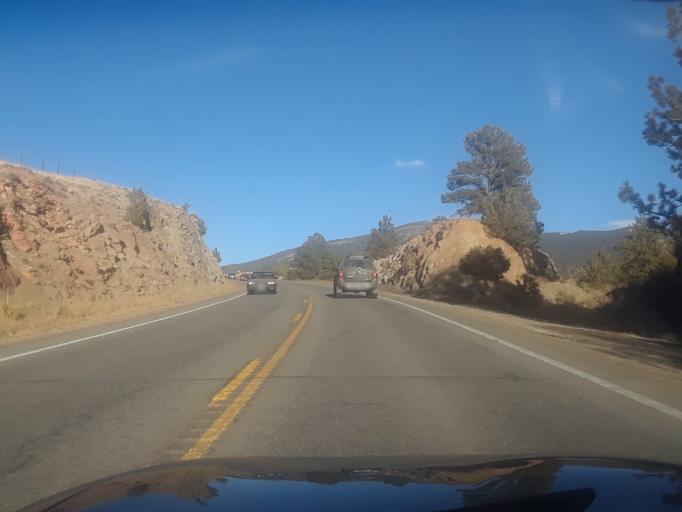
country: US
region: Colorado
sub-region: Chaffee County
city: Buena Vista
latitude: 38.8413
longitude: -105.9985
